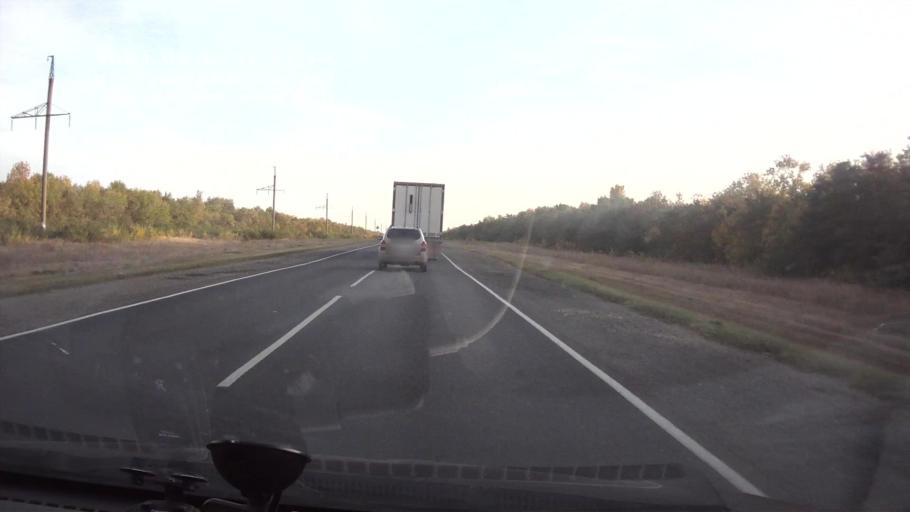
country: RU
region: Saratov
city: Krasnoarmeysk
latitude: 51.1272
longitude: 45.6506
